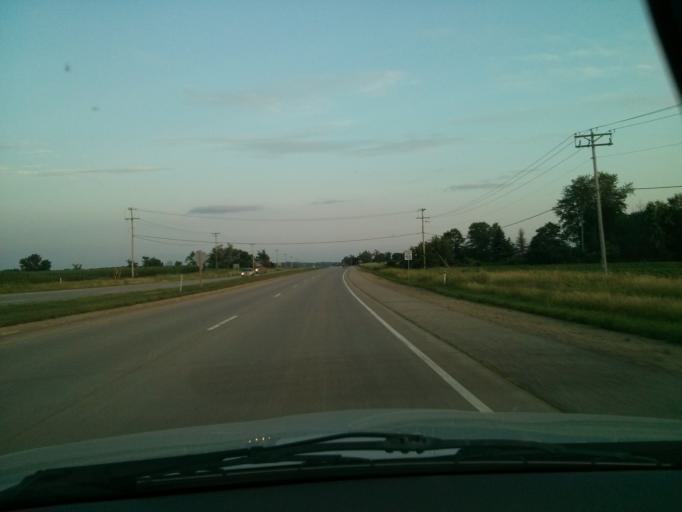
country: US
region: Wisconsin
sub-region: Saint Croix County
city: North Hudson
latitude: 44.9867
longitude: -92.6802
